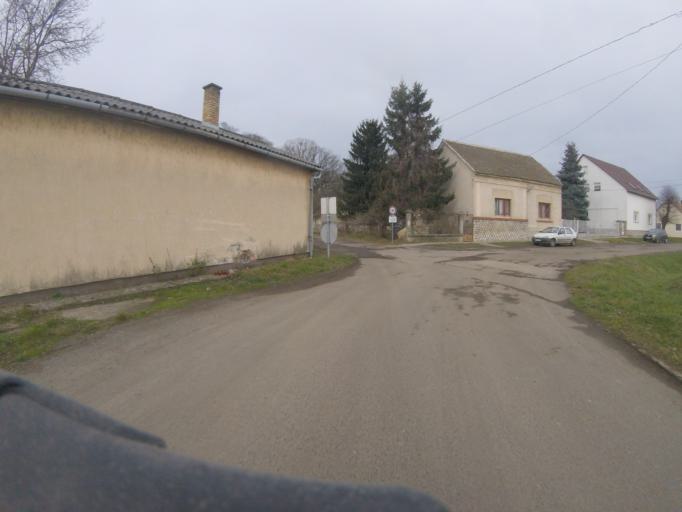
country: HU
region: Tolna
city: Dombovar
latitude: 46.3648
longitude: 18.1396
